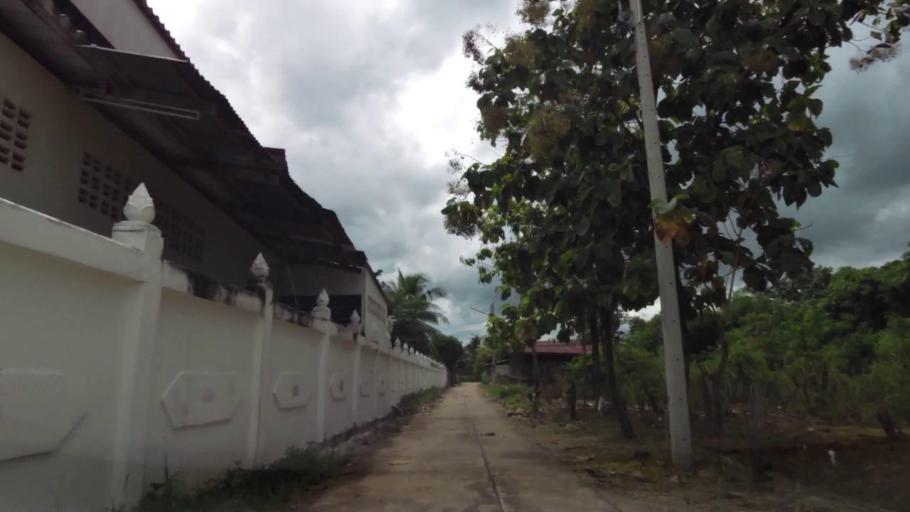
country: TH
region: Nakhon Sawan
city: Phai Sali
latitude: 15.6008
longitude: 100.6519
